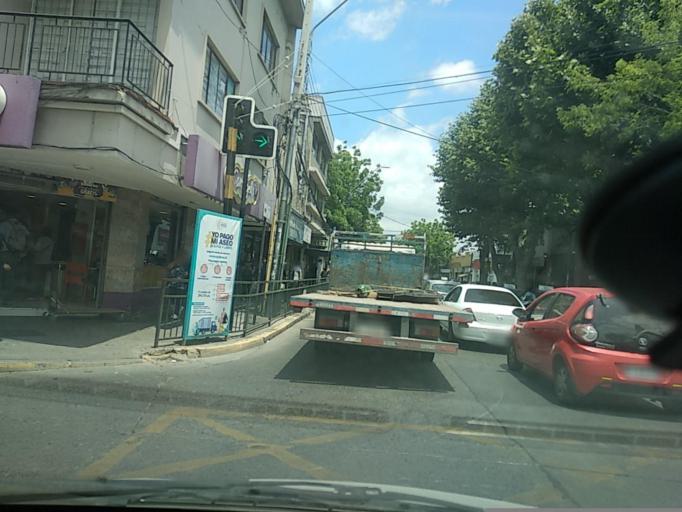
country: CL
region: Valparaiso
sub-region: Provincia de Marga Marga
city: Quilpue
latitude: -33.0470
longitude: -71.4419
